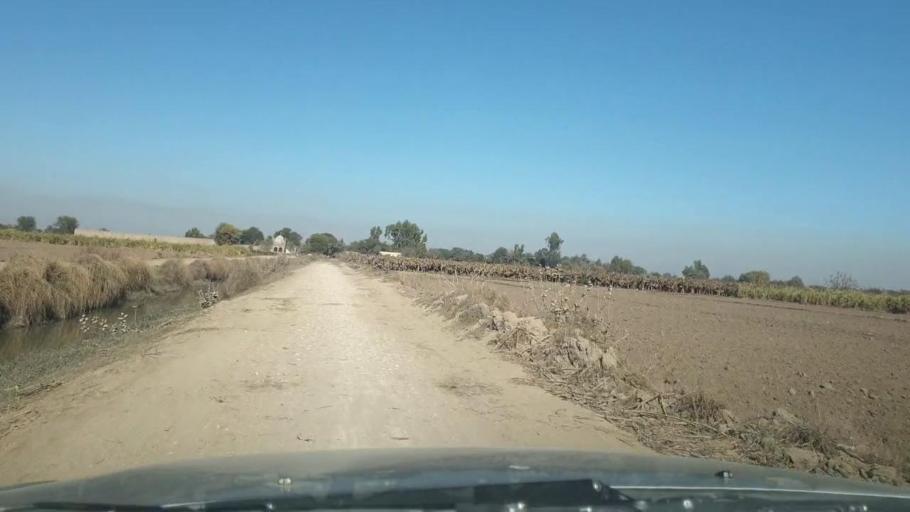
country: PK
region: Sindh
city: Ghotki
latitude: 28.0402
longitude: 69.2467
